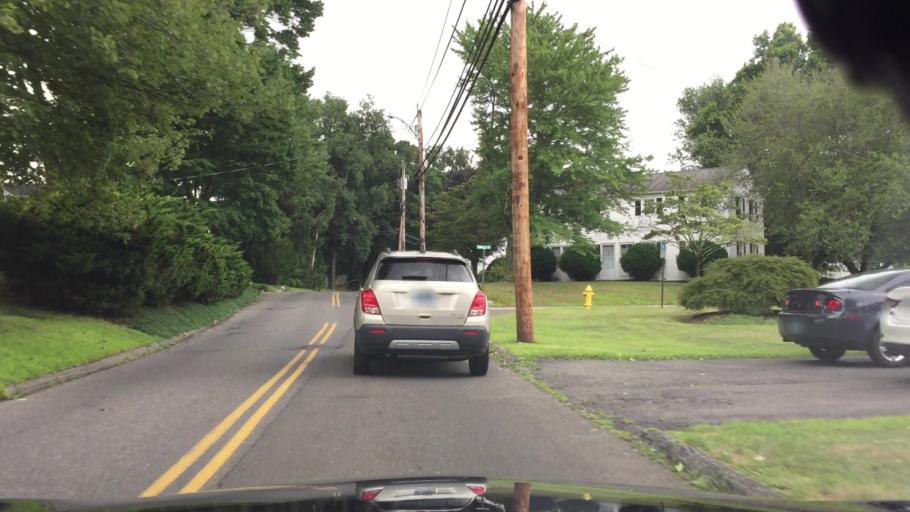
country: US
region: Connecticut
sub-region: New Haven County
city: City of Milford (balance)
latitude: 41.2013
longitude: -73.0864
